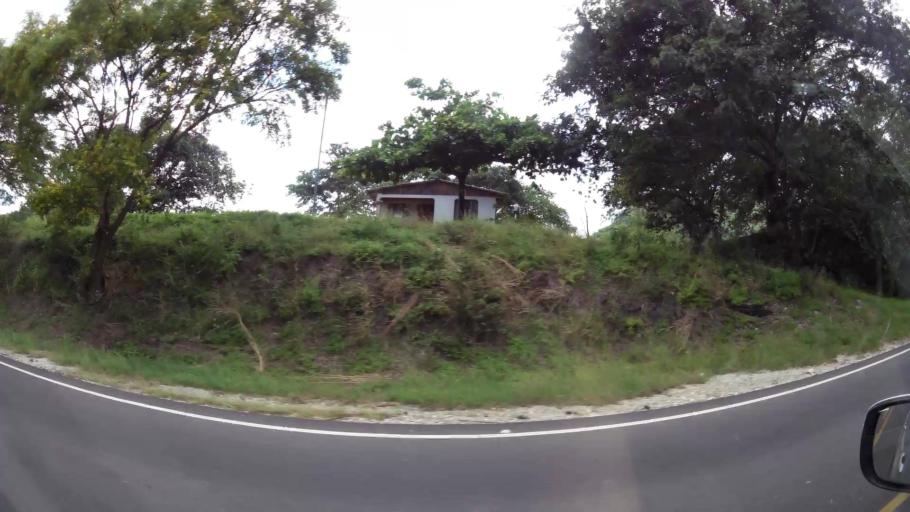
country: CR
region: Guanacaste
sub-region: Canton de Nicoya
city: Nicoya
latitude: 10.1697
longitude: -85.3022
